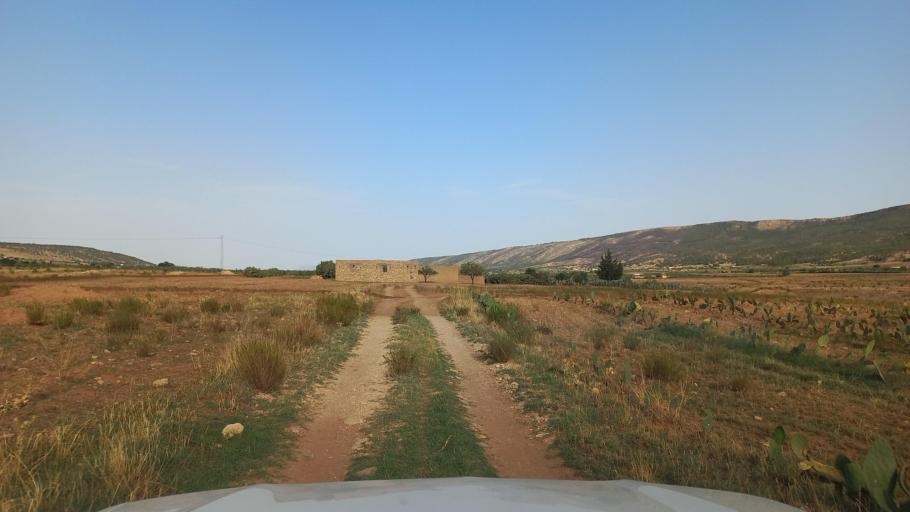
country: TN
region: Al Qasrayn
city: Kasserine
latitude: 35.3581
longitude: 8.8550
